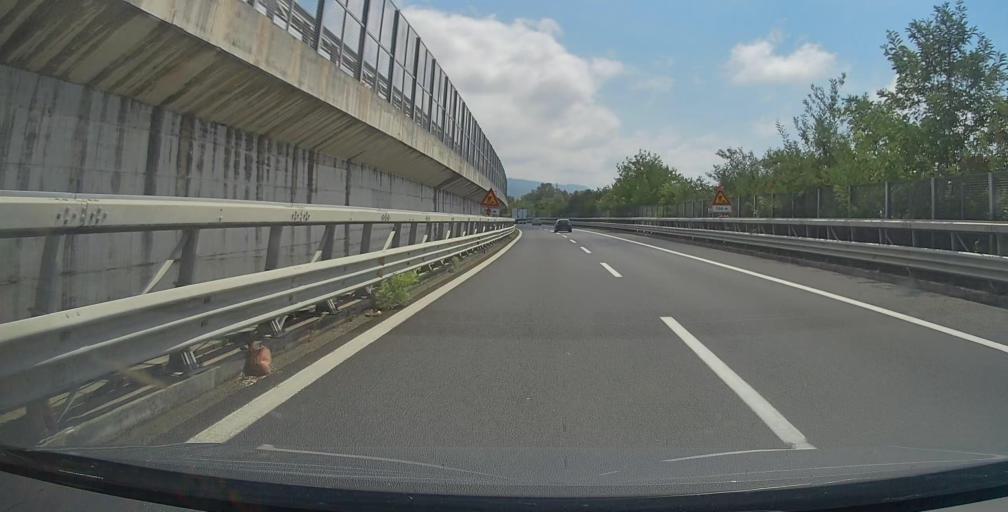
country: IT
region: Calabria
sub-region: Provincia di Vibo-Valentia
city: Pizzo
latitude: 38.7864
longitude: 16.2199
